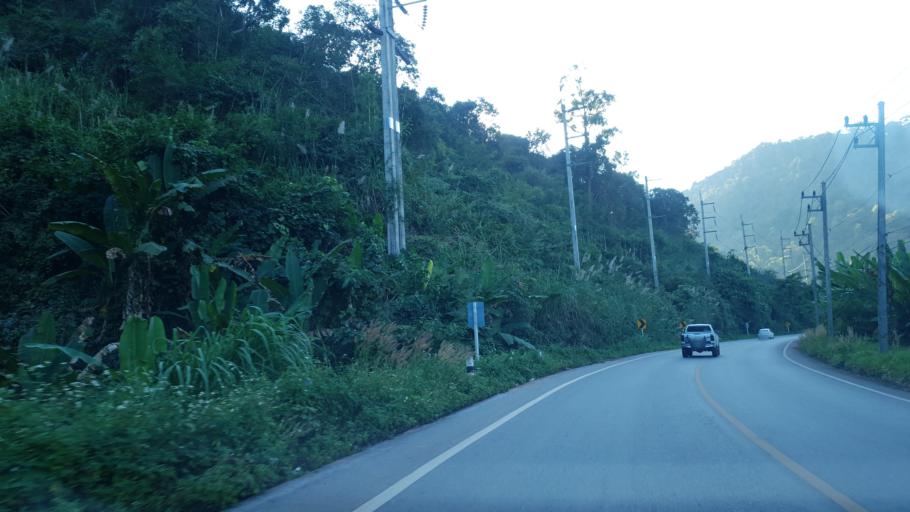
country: TH
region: Loei
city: Dan Sai
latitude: 17.2244
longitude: 101.0329
